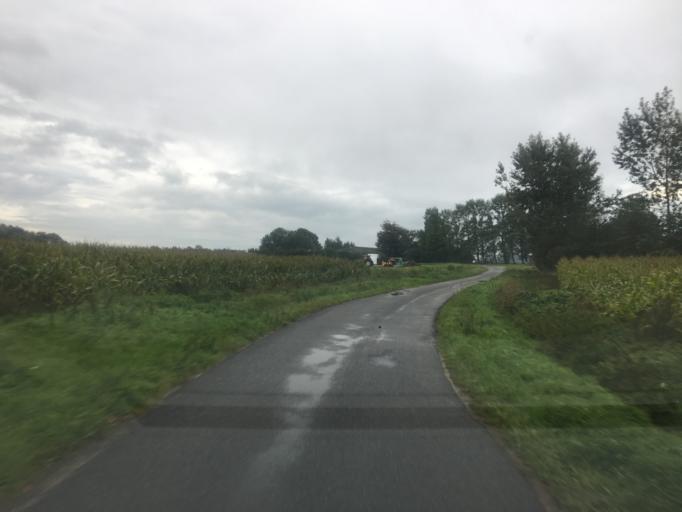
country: DK
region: South Denmark
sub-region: Tonder Kommune
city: Logumkloster
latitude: 54.9811
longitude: 8.9603
